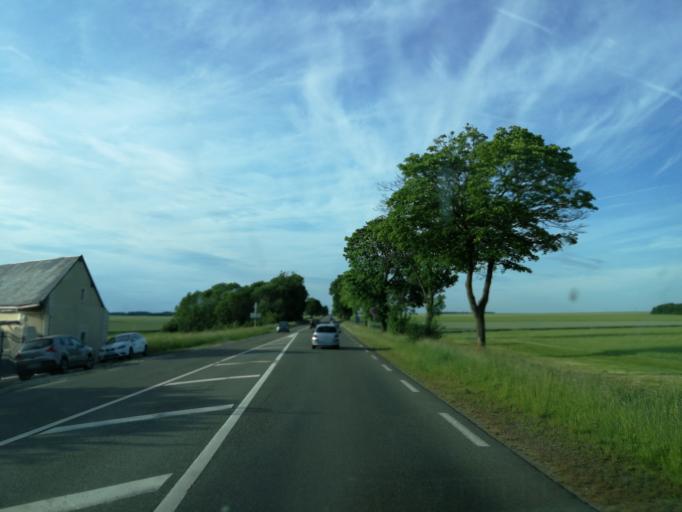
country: FR
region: Centre
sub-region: Departement d'Eure-et-Loir
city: Dammarie
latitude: 48.2803
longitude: 1.4183
